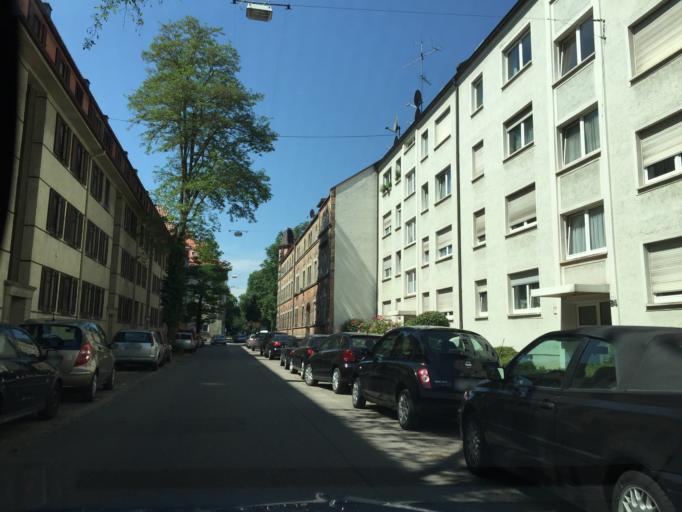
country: DE
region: Baden-Wuerttemberg
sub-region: Tuebingen Region
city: Ulm
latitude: 48.3929
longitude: 9.9945
